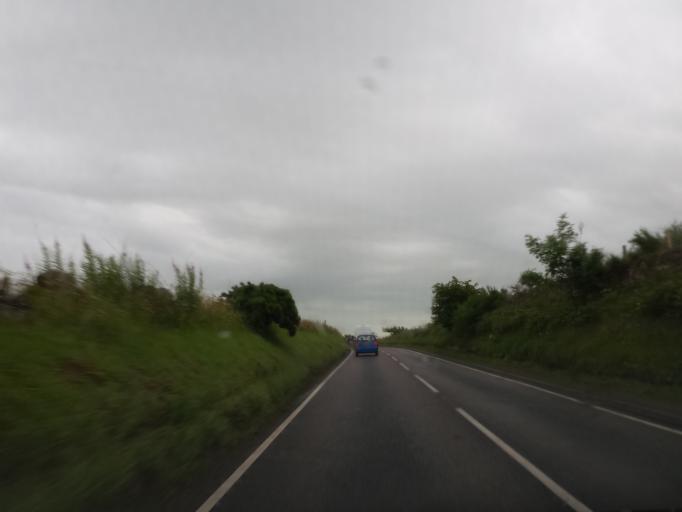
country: GB
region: Scotland
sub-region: Fife
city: Leuchars
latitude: 56.3883
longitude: -2.8983
